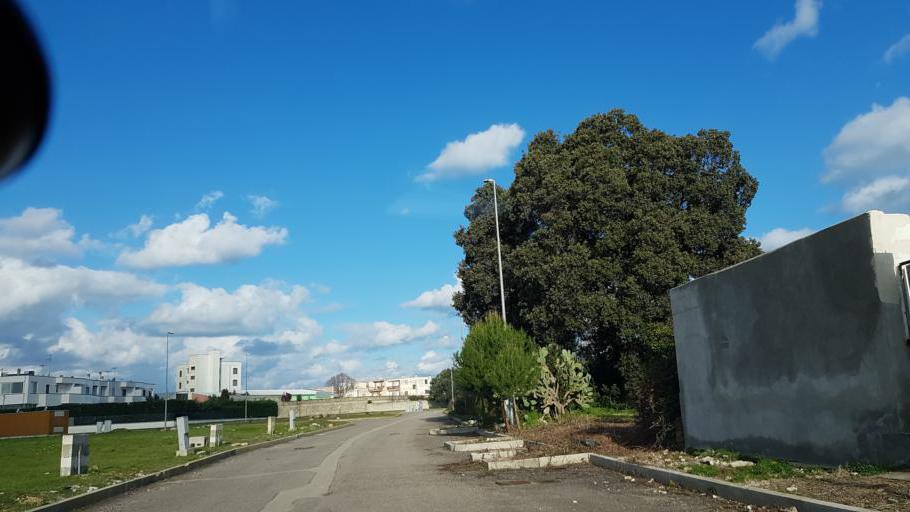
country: IT
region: Apulia
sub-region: Provincia di Brindisi
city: Brindisi
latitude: 40.6430
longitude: 17.9207
